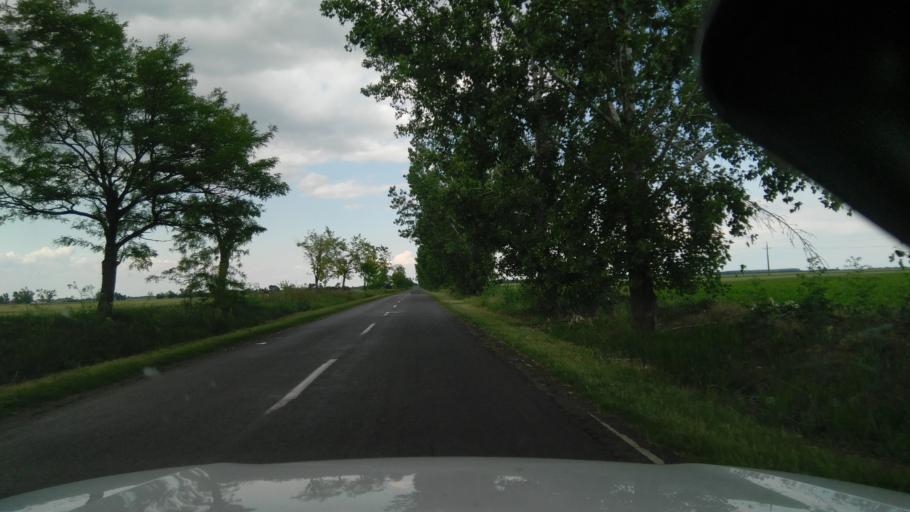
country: HU
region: Bekes
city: Magyarbanhegyes
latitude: 46.4568
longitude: 21.0014
